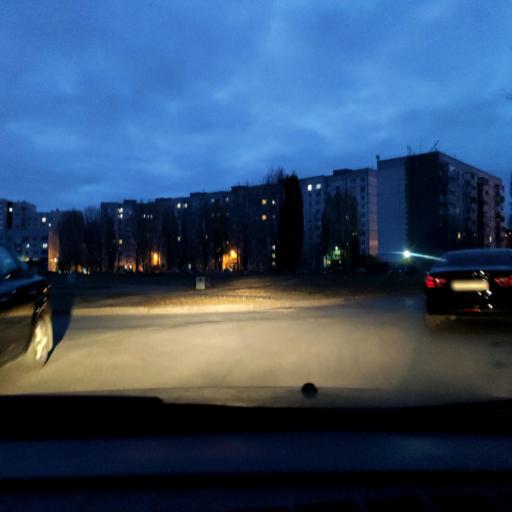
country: RU
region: Samara
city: Tol'yatti
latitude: 53.5446
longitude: 49.3259
